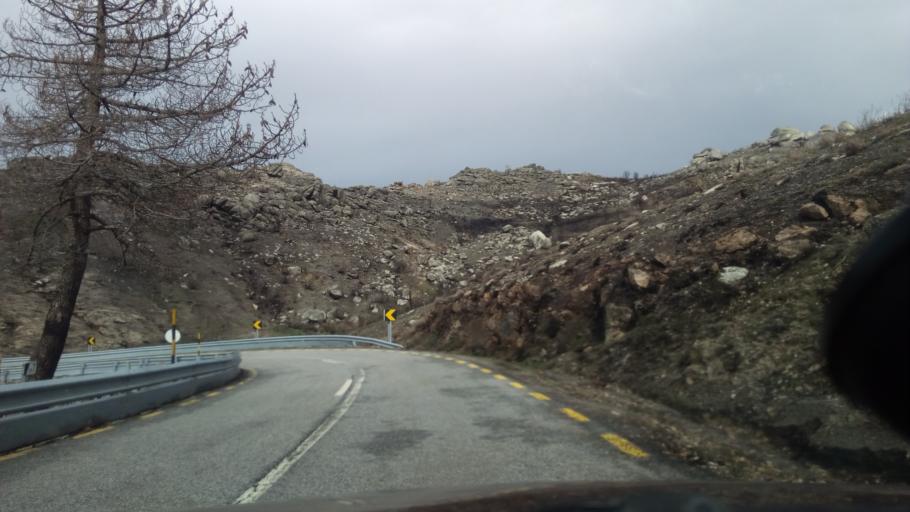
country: PT
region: Guarda
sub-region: Manteigas
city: Manteigas
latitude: 40.4208
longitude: -7.6156
